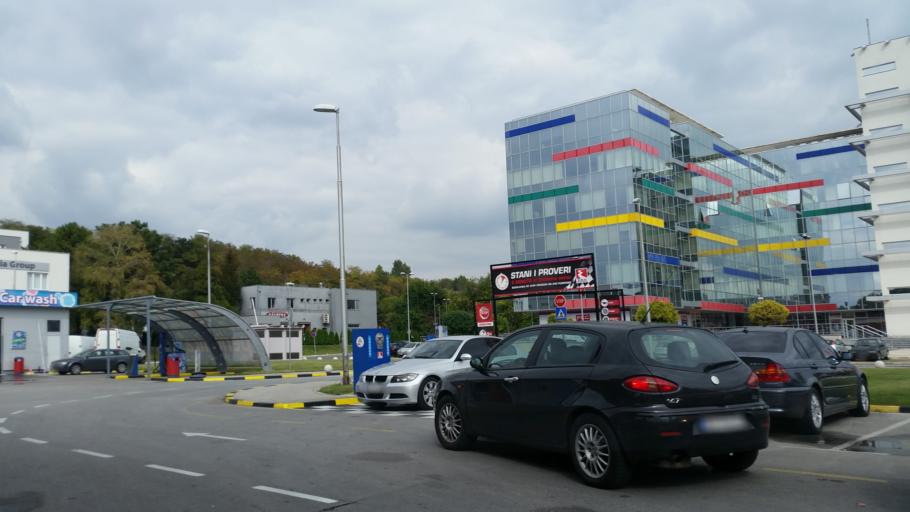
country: RS
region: Central Serbia
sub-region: Belgrade
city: Zemun
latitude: 44.8128
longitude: 20.3896
